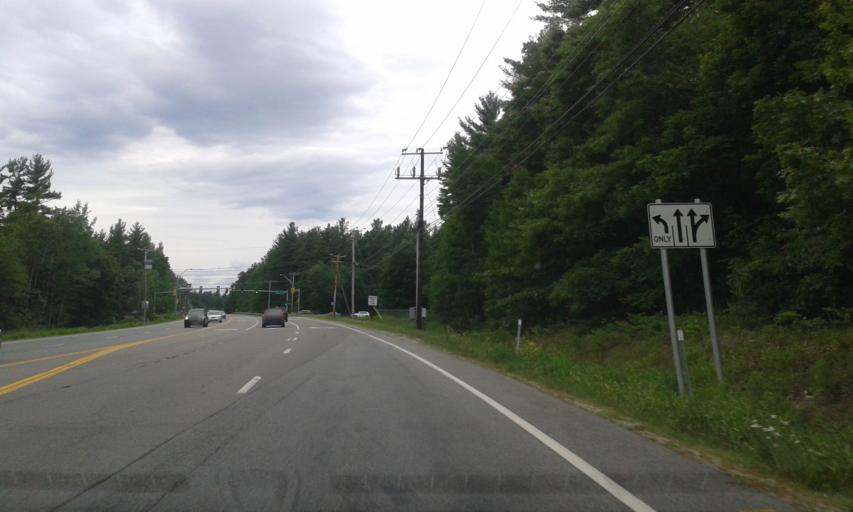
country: US
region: New Hampshire
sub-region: Hillsborough County
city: Litchfield
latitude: 42.8199
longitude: -71.5164
